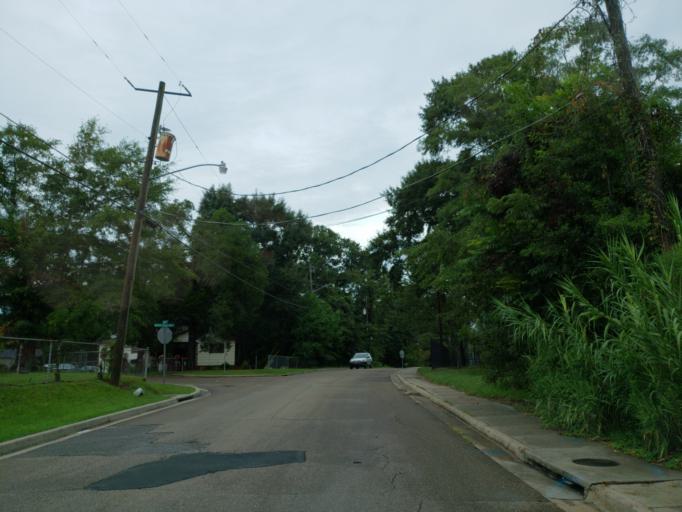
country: US
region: Mississippi
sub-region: Forrest County
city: Hattiesburg
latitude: 31.3135
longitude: -89.2994
